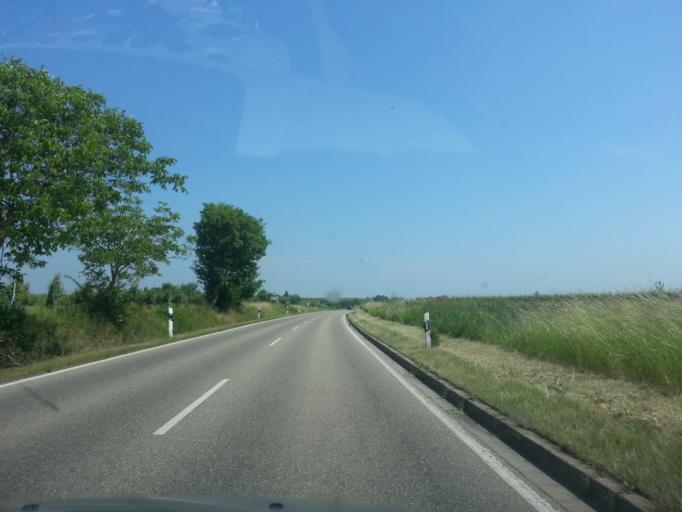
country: DE
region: Rheinland-Pfalz
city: Kallstadt
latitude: 49.4883
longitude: 8.1906
